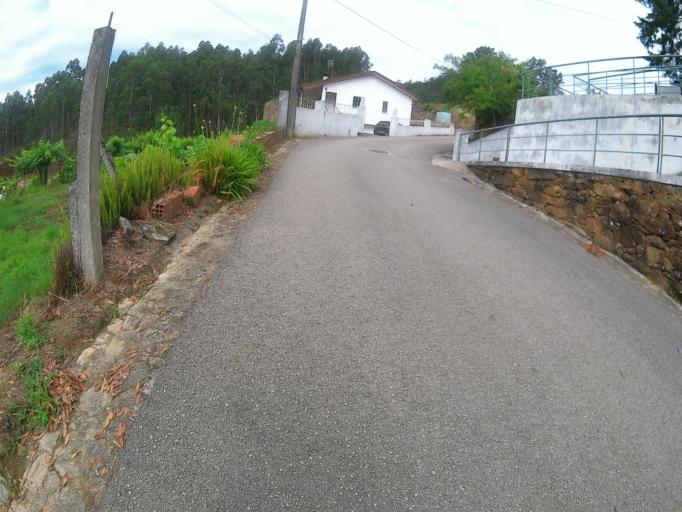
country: PT
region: Aveiro
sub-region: Albergaria-A-Velha
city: Branca
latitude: 40.7574
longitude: -8.4254
